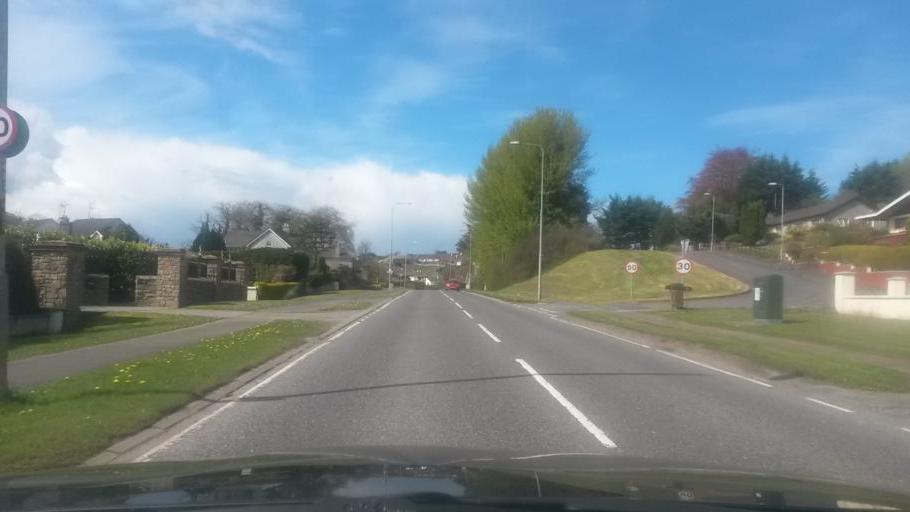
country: GB
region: Northern Ireland
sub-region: Fermanagh District
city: Enniskillen
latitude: 54.3586
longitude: -7.6716
